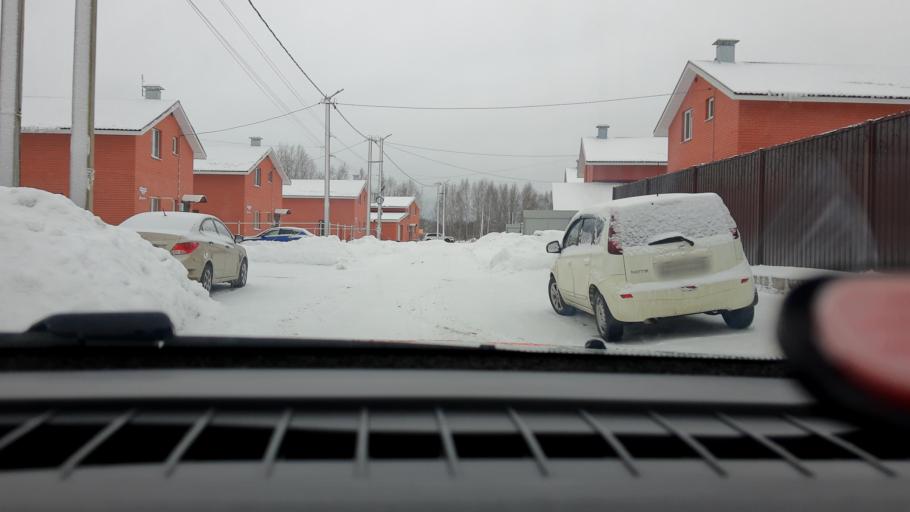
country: RU
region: Nizjnij Novgorod
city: Afonino
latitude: 56.1983
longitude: 44.0682
